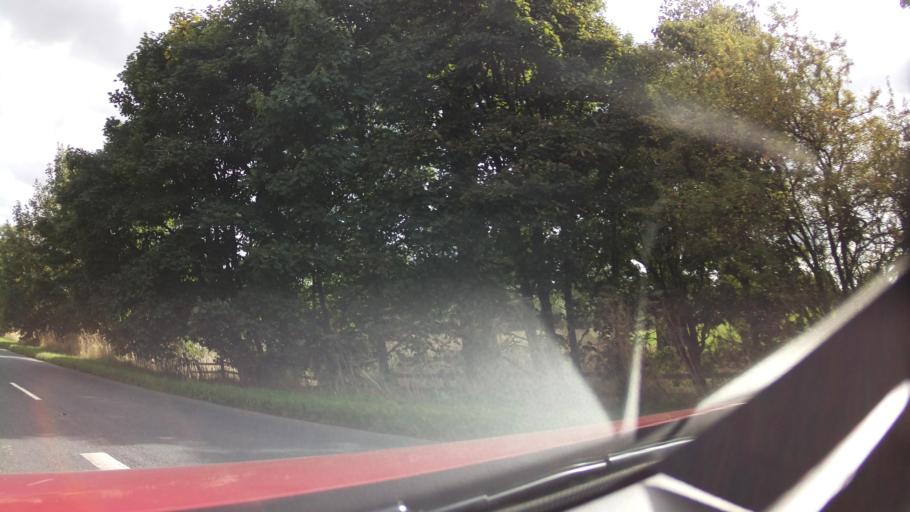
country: GB
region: England
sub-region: North Yorkshire
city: Ripon
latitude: 54.1974
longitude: -1.5790
